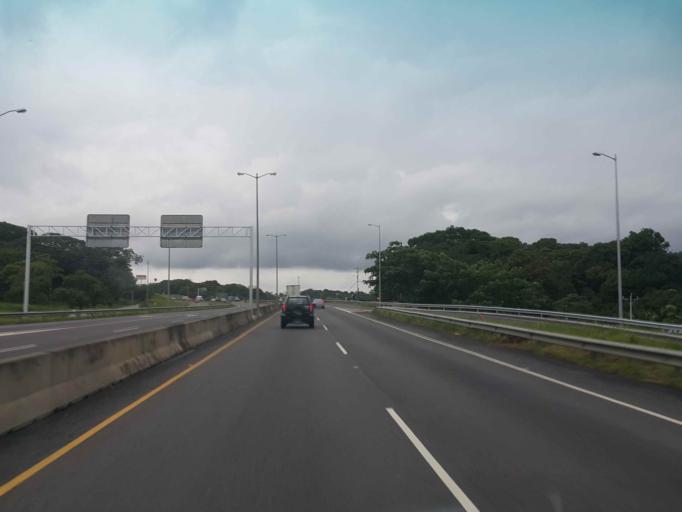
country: CR
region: Alajuela
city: Atenas
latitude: 9.9437
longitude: -84.3761
